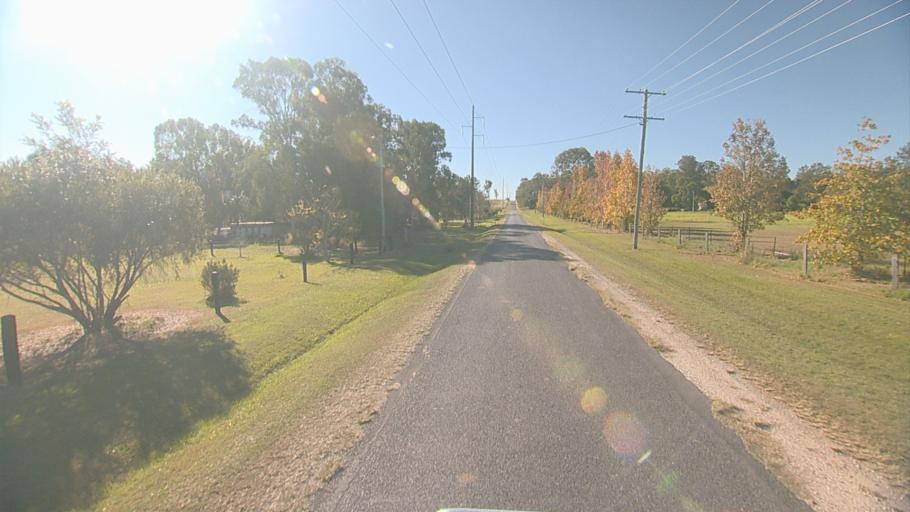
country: AU
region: Queensland
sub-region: Logan
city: Chambers Flat
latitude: -27.7784
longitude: 153.0583
